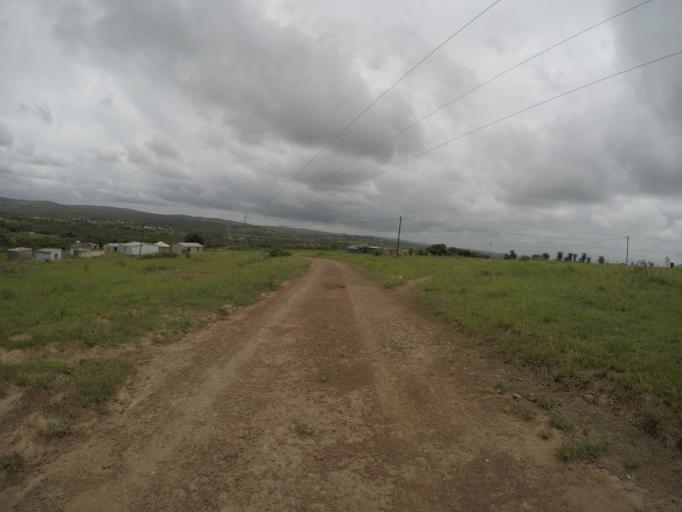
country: ZA
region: KwaZulu-Natal
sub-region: uThungulu District Municipality
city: Empangeni
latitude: -28.6003
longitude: 31.8463
